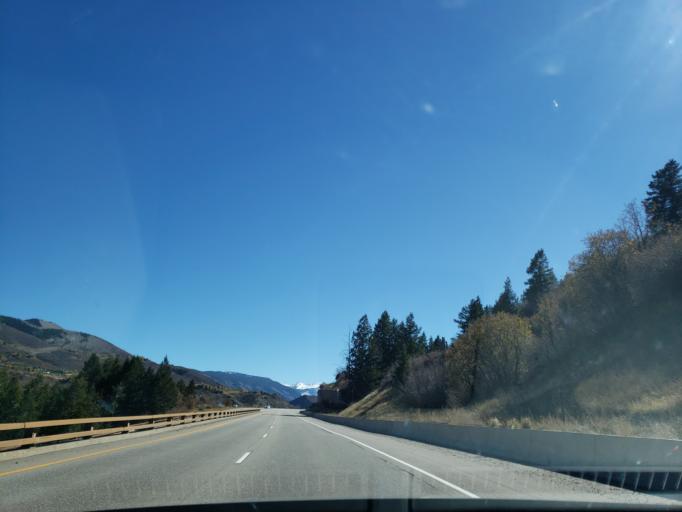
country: US
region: Colorado
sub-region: Pitkin County
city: Snowmass Village
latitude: 39.2427
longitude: -106.8805
